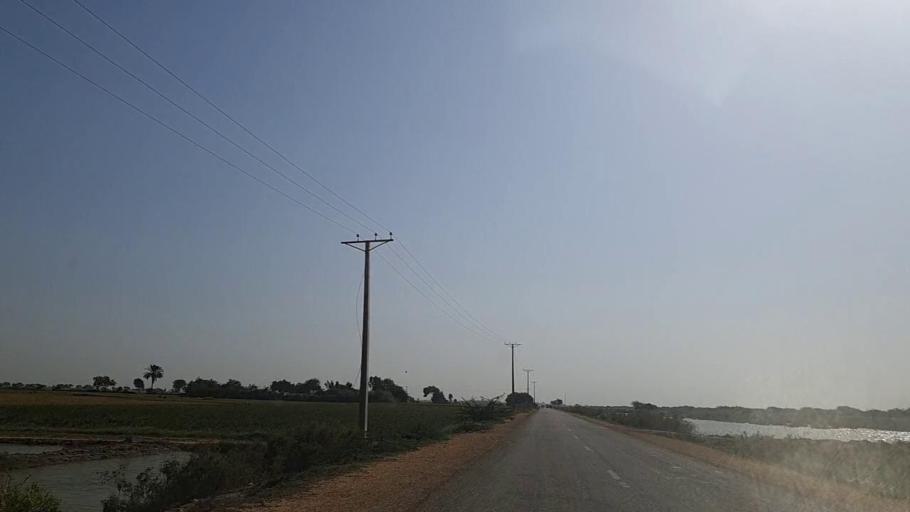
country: PK
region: Sindh
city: Mirpur Batoro
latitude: 24.5423
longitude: 68.2802
